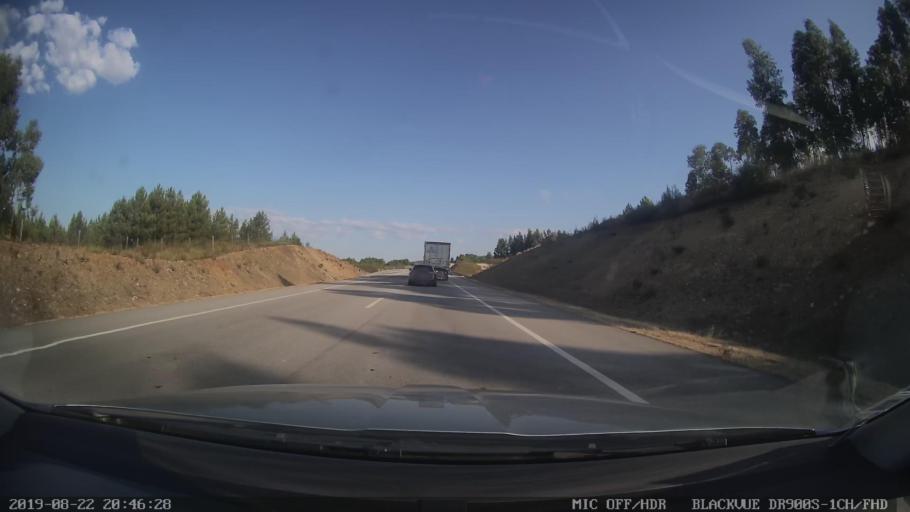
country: PT
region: Castelo Branco
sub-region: Proenca-A-Nova
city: Proenca-a-Nova
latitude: 39.7268
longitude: -7.8768
